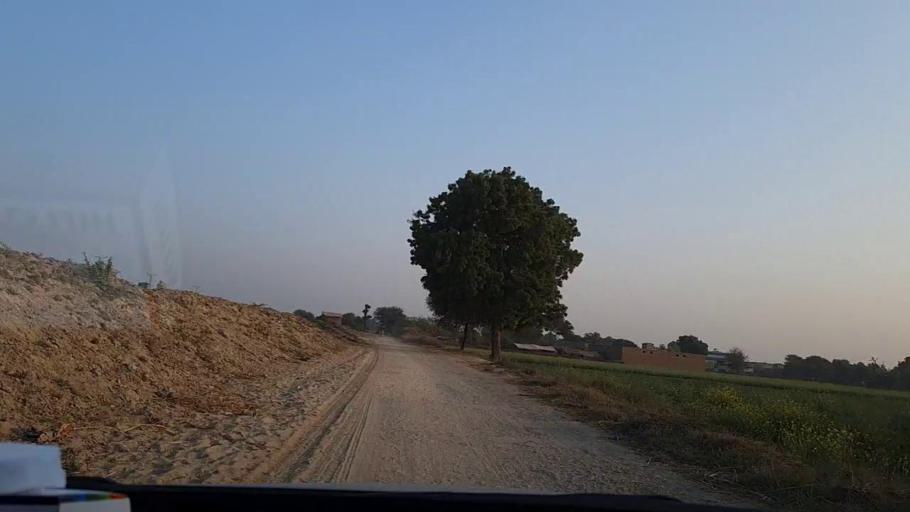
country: PK
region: Sindh
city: Tando Ghulam Ali
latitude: 25.1768
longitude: 68.9257
